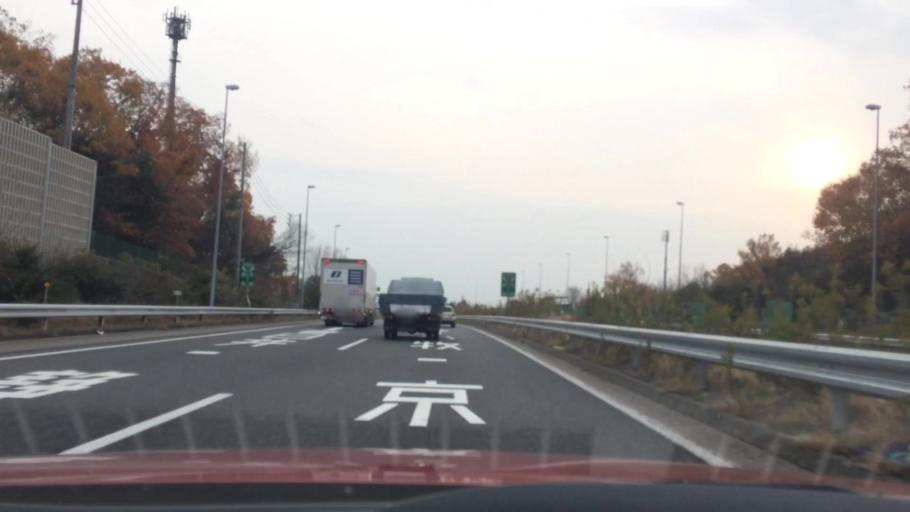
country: JP
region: Aichi
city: Kasugai
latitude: 35.2896
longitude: 136.9817
